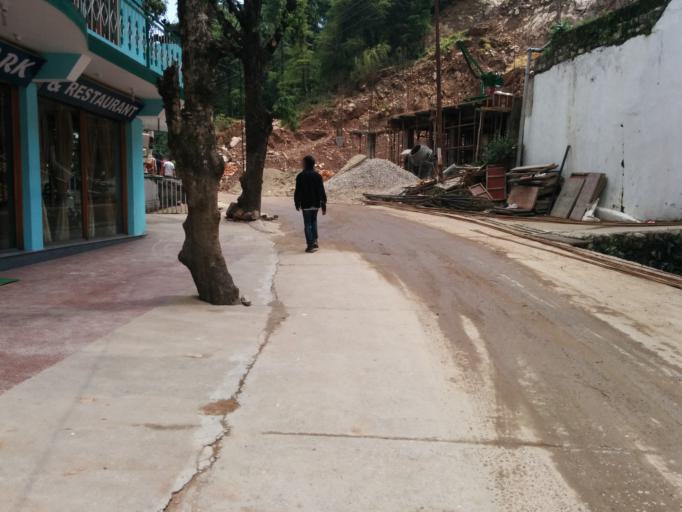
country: IN
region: Himachal Pradesh
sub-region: Kangra
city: Dharmsala
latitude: 32.2428
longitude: 76.3321
